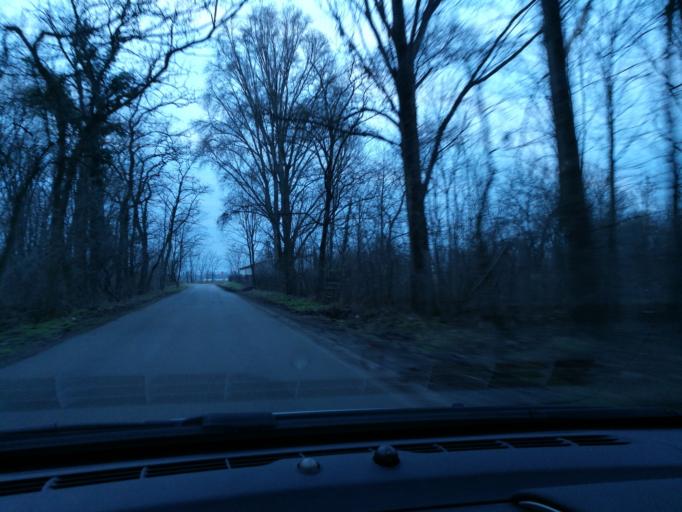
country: HU
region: Szabolcs-Szatmar-Bereg
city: Nyiregyhaza
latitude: 47.9829
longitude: 21.7066
